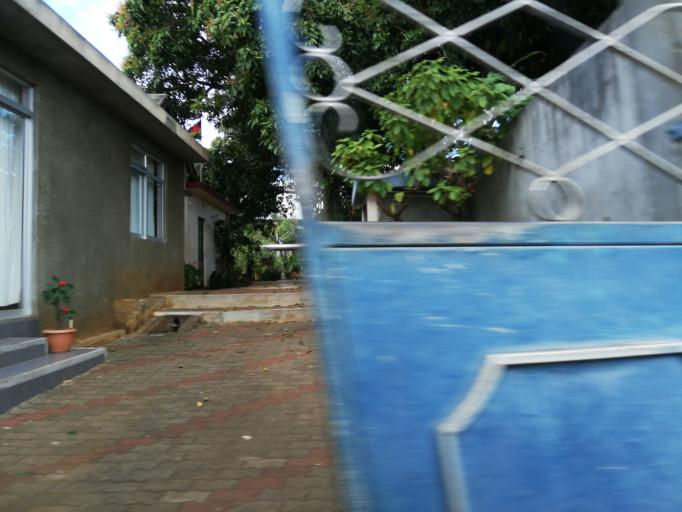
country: MU
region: Black River
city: Gros Cailloux
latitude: -20.2293
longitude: 57.4538
